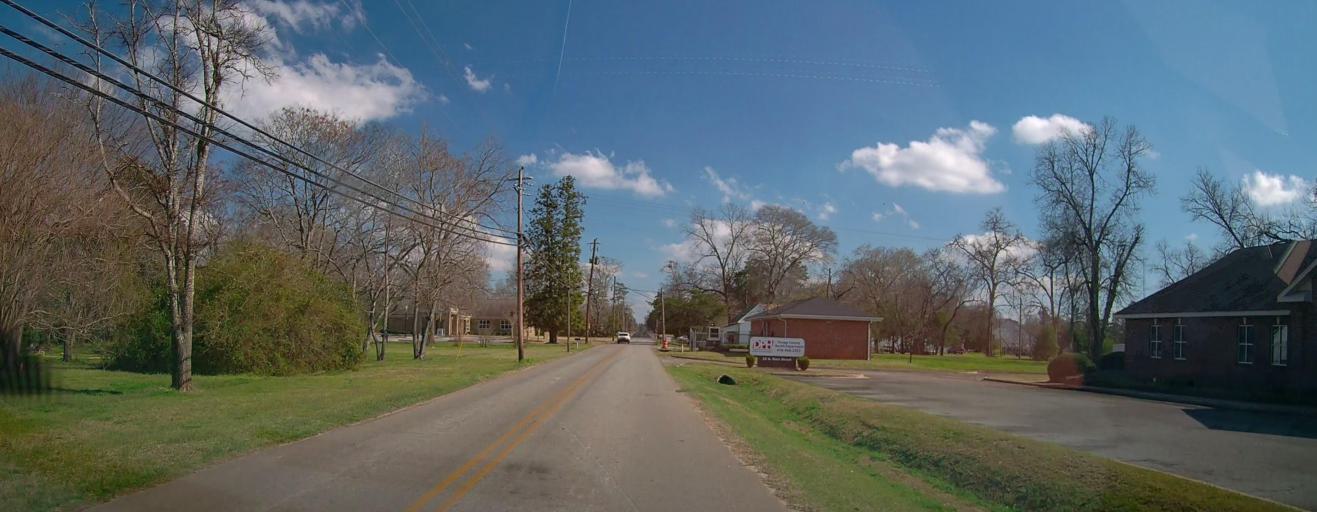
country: US
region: Georgia
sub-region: Twiggs County
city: Jeffersonville
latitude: 32.6890
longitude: -83.3443
